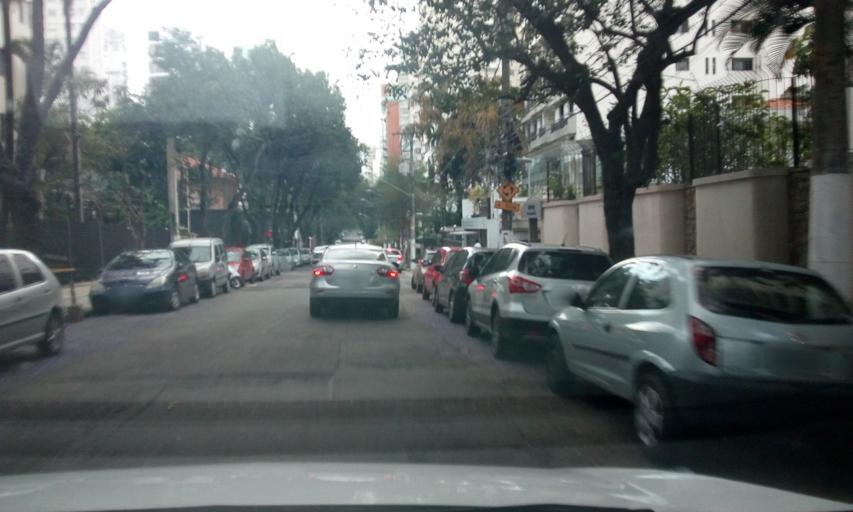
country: BR
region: Sao Paulo
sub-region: Sao Paulo
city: Sao Paulo
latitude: -23.6059
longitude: -46.6552
